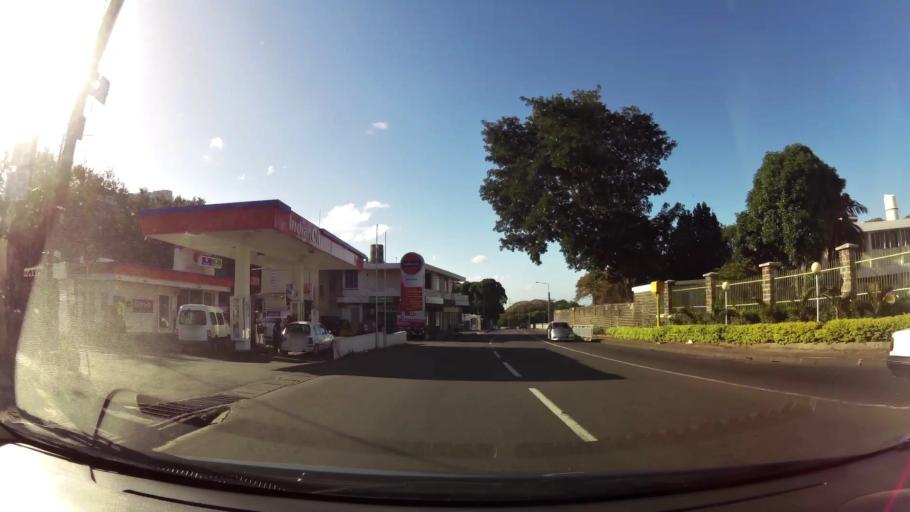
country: MU
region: Moka
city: Pailles
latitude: -20.1784
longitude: 57.4703
